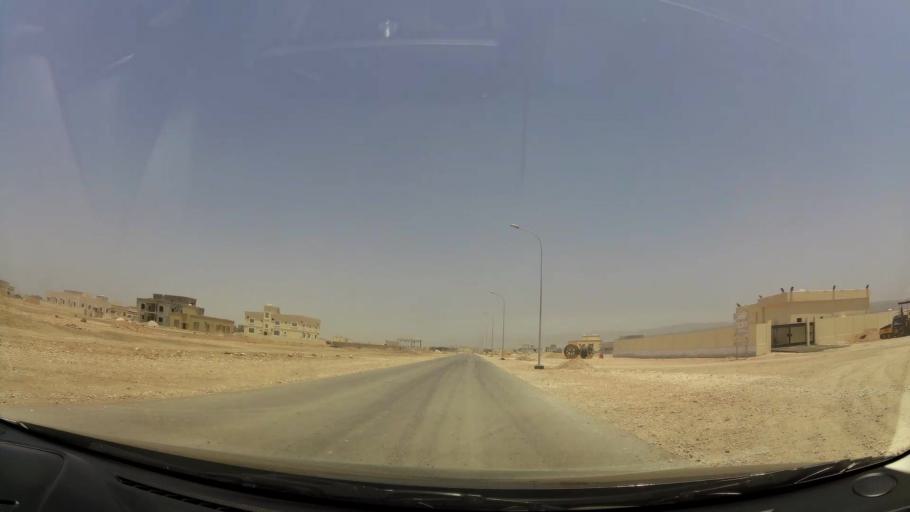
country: OM
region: Zufar
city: Salalah
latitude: 17.0977
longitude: 54.1811
